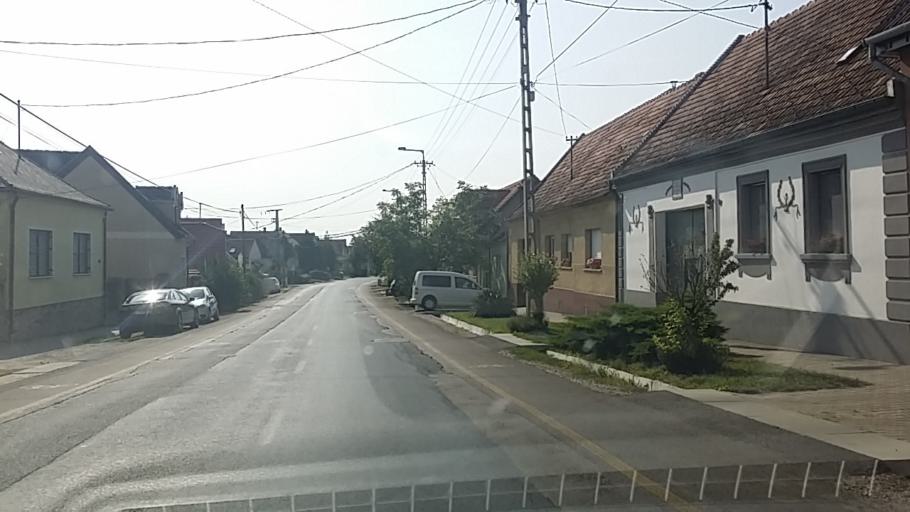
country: HU
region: Gyor-Moson-Sopron
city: Fertorakos
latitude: 47.7239
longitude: 16.6478
